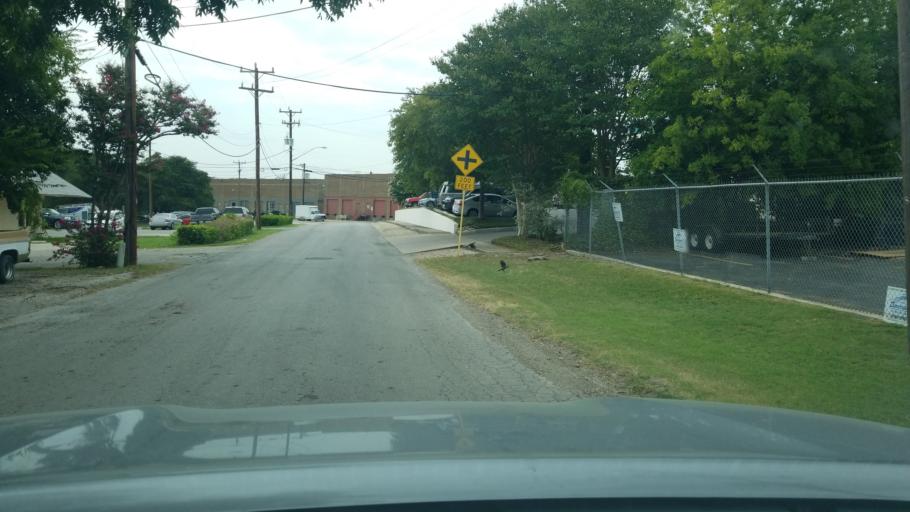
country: US
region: Texas
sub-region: Bexar County
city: Castle Hills
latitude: 29.5296
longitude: -98.4910
